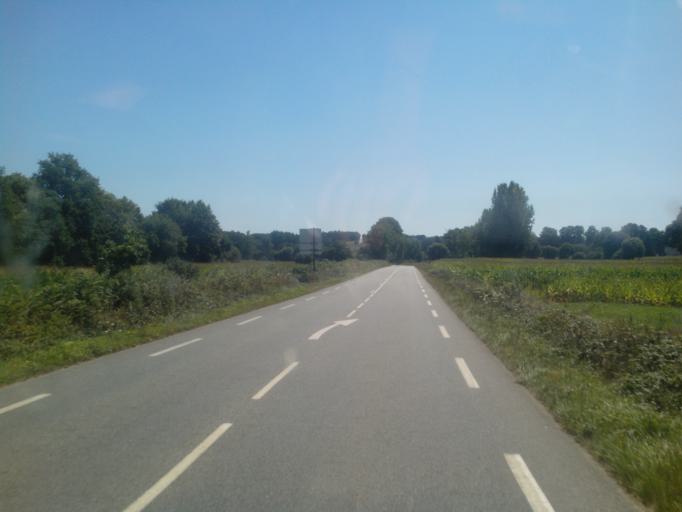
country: FR
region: Brittany
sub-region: Departement du Morbihan
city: Josselin
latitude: 47.9373
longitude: -2.5400
